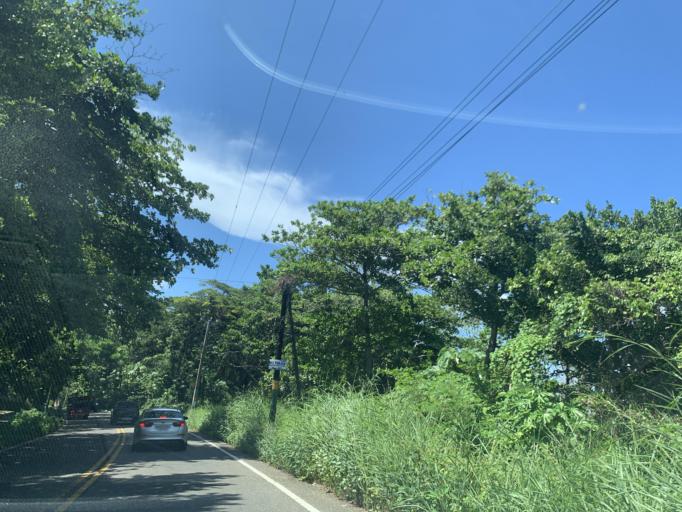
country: DO
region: Maria Trinidad Sanchez
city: Cabrera
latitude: 19.6548
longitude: -69.9343
